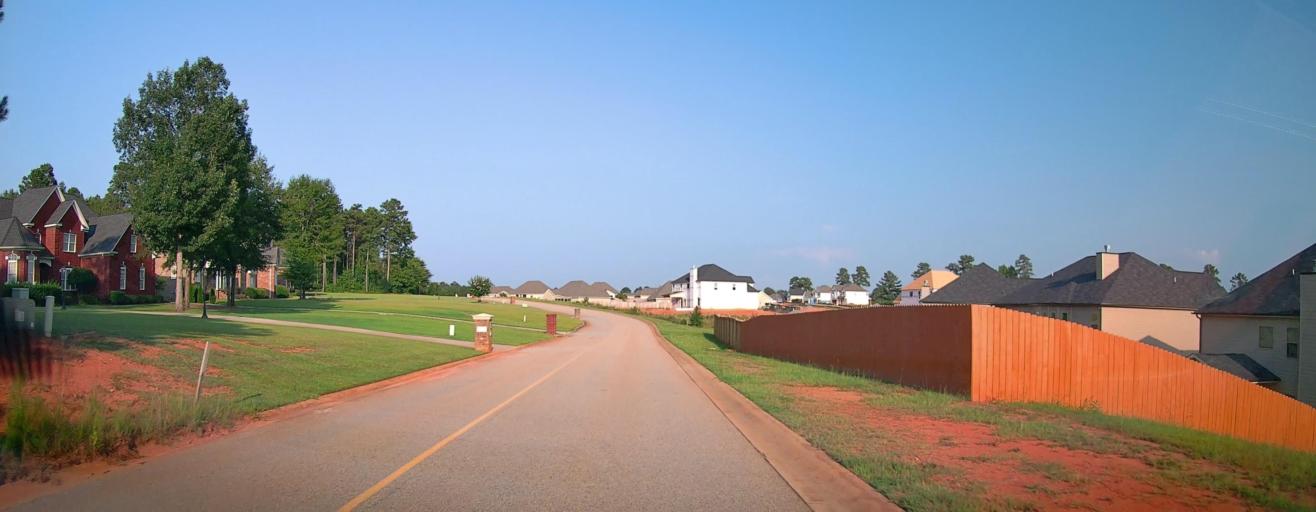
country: US
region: Georgia
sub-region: Bibb County
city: West Point
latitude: 32.8844
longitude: -83.8267
